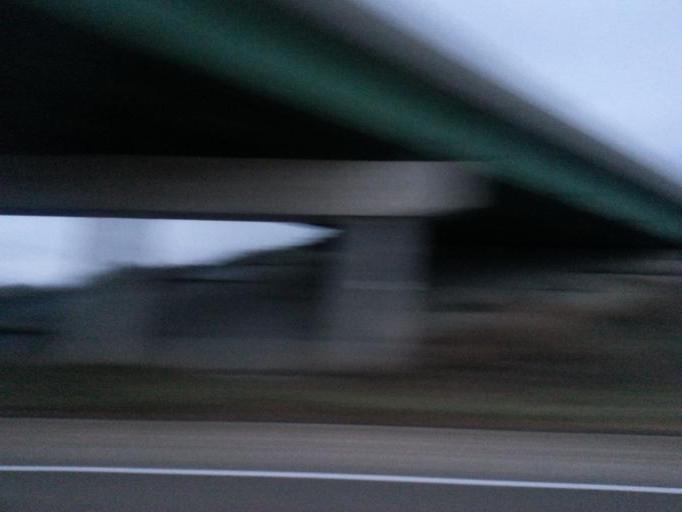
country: US
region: Iowa
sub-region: Black Hawk County
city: La Porte City
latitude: 42.4133
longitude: -92.1716
